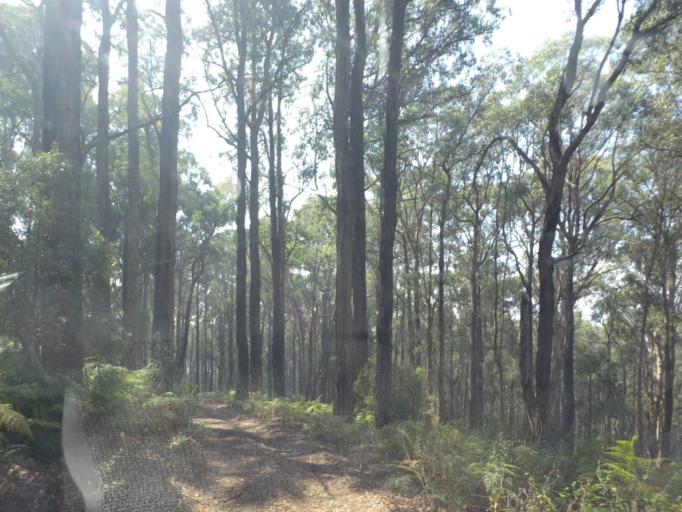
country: AU
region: Victoria
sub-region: Yarra Ranges
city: Healesville
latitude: -37.5616
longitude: 145.6337
